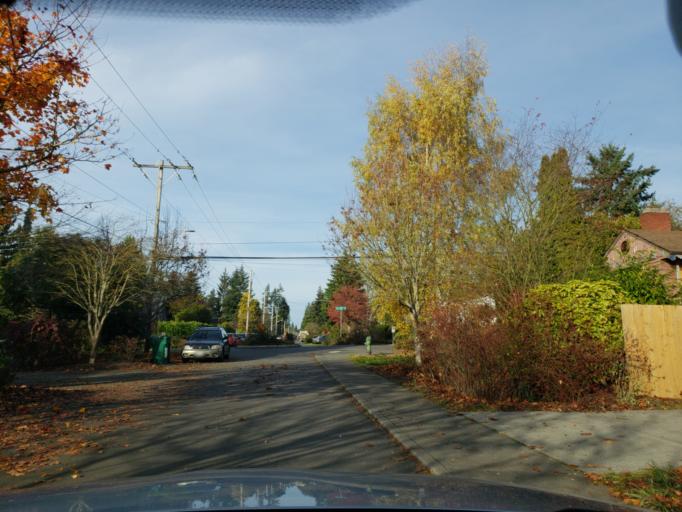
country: US
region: Washington
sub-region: King County
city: Shoreline
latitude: 47.7084
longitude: -122.3581
